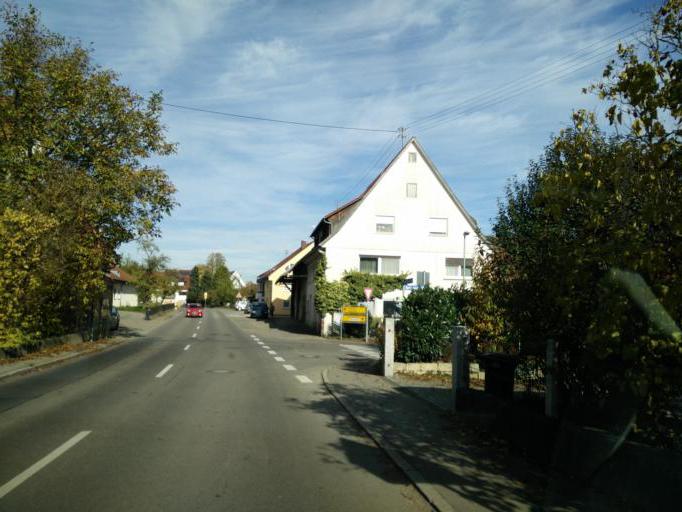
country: DE
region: Baden-Wuerttemberg
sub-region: Tuebingen Region
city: Gomaringen
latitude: 48.4859
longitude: 9.1067
